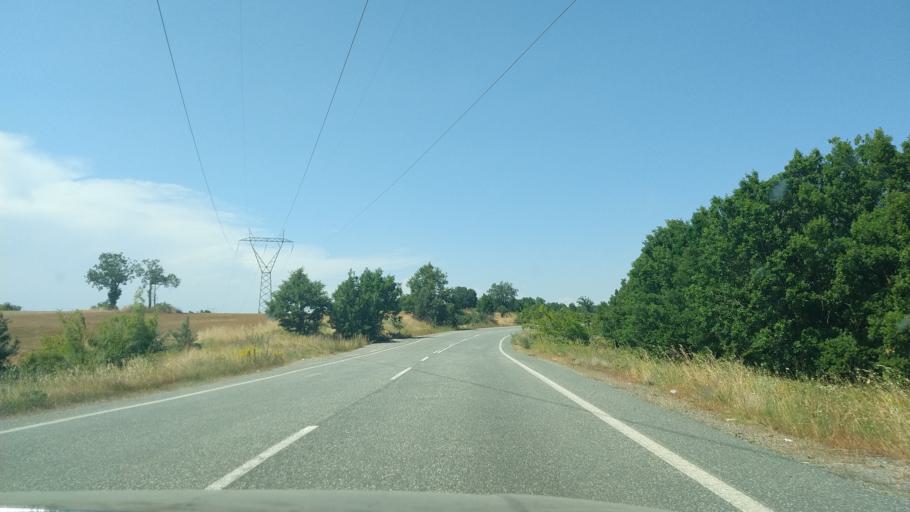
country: GR
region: West Macedonia
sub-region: Nomos Grevenon
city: Grevena
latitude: 40.0613
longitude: 21.4676
